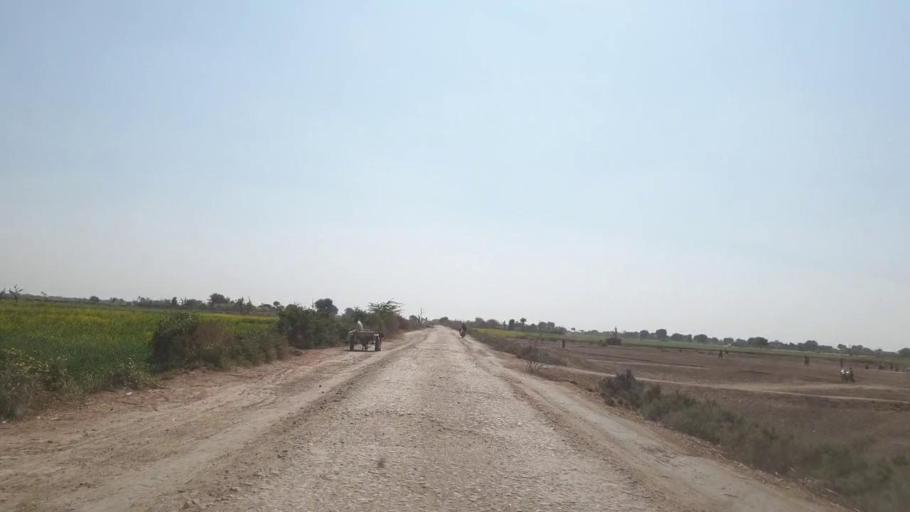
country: PK
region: Sindh
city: Mirpur Khas
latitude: 25.7411
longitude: 69.0823
